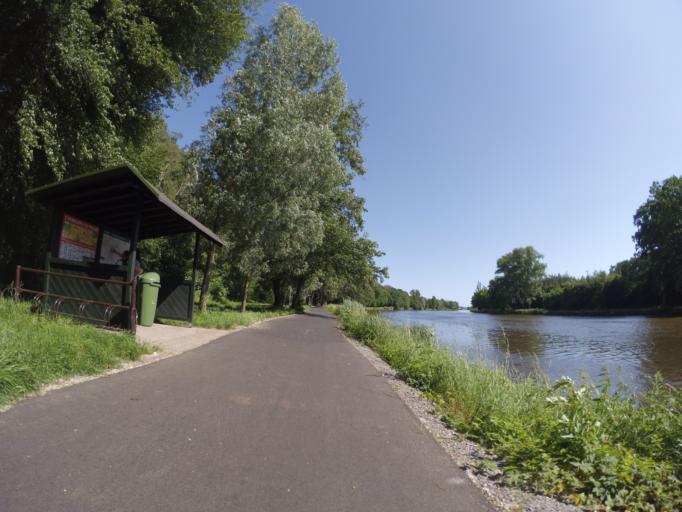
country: CZ
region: Central Bohemia
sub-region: Okres Nymburk
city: Nymburk
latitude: 50.1784
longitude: 15.0737
